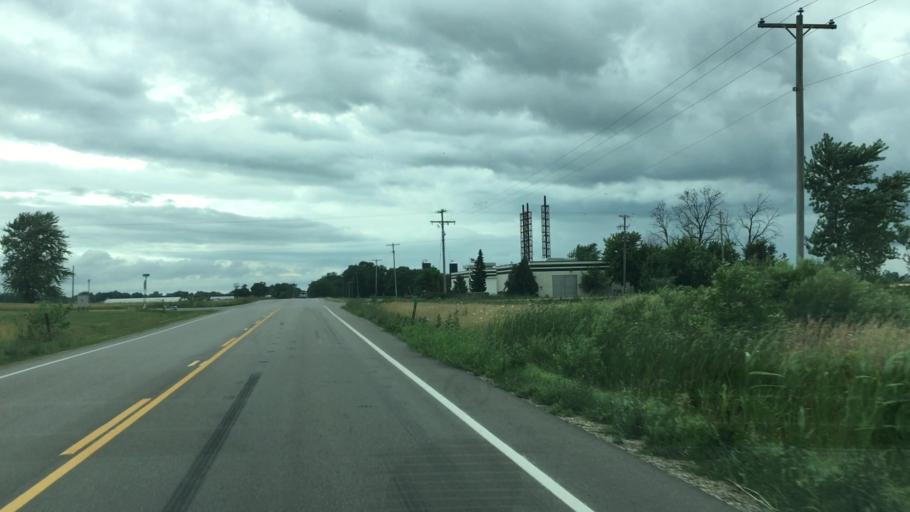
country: US
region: Michigan
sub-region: Ottawa County
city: Zeeland
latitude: 42.7827
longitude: -85.9200
